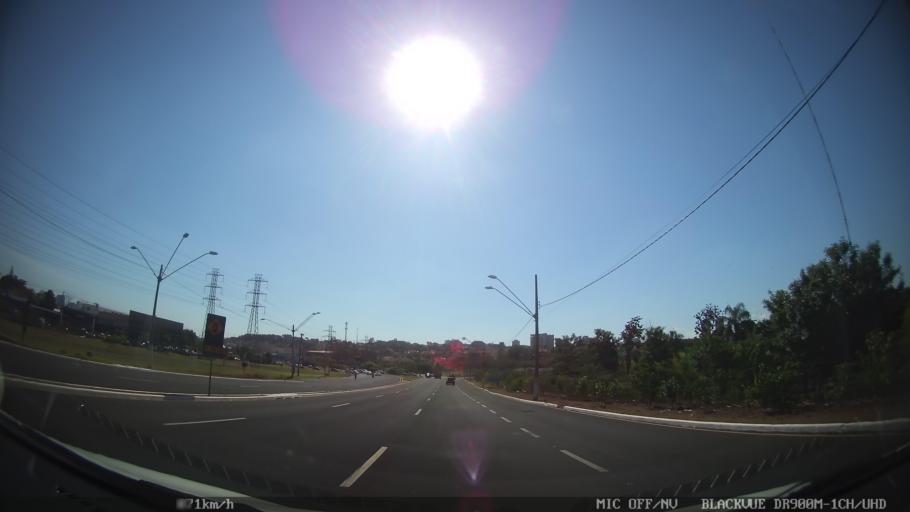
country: BR
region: Sao Paulo
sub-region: Ribeirao Preto
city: Ribeirao Preto
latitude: -21.2136
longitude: -47.7737
